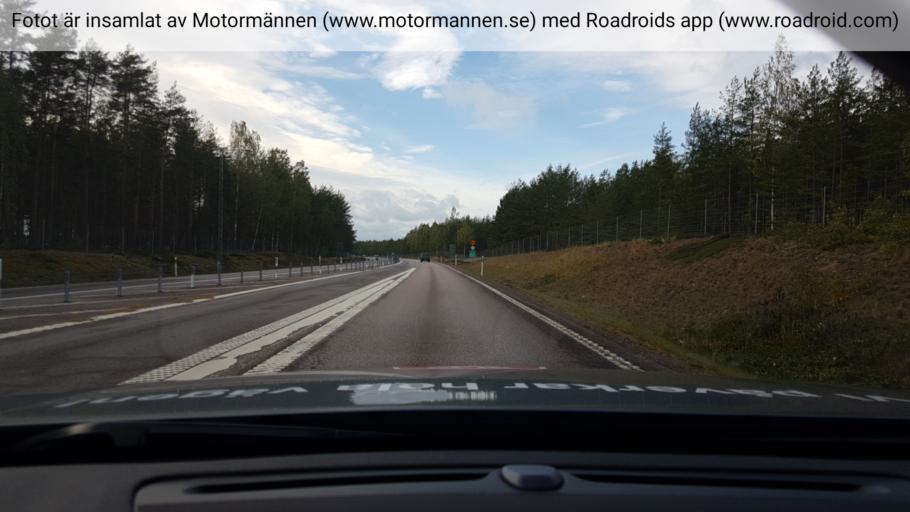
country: SE
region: Vaermland
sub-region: Karlstads Kommun
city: Valberg
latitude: 59.3868
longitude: 13.2316
